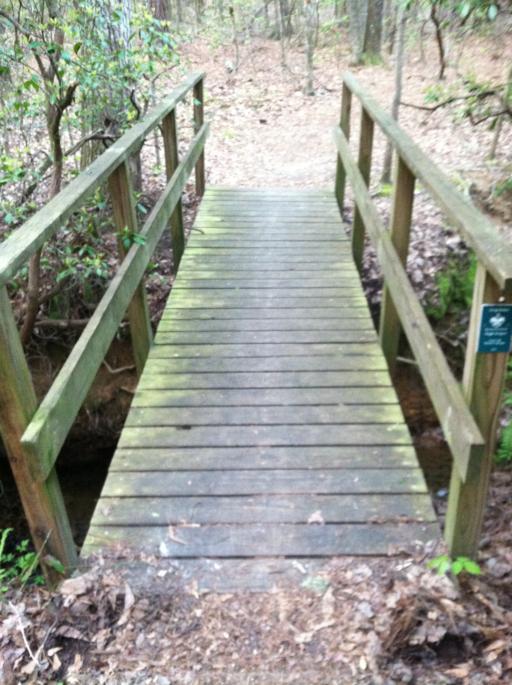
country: US
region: Georgia
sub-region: Harris County
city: Pine Mountain
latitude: 32.8415
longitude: -84.8361
